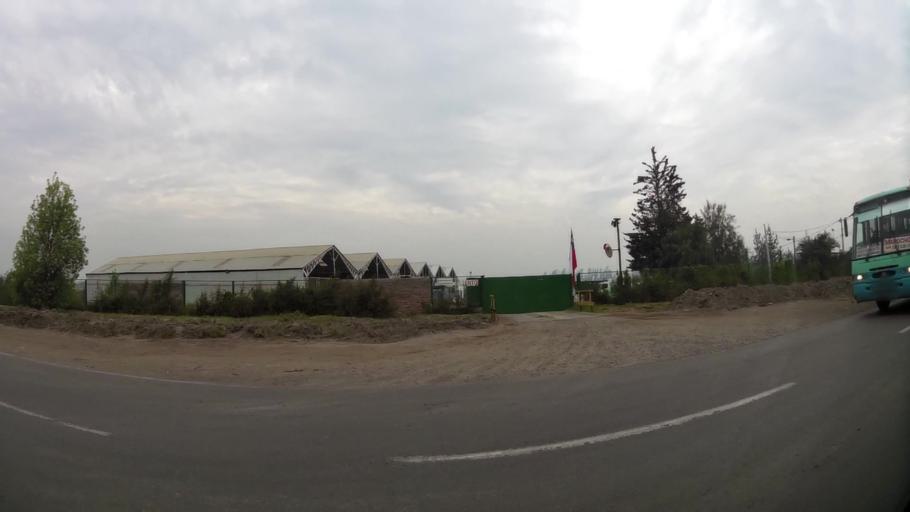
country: CL
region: Santiago Metropolitan
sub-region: Provincia de Chacabuco
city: Chicureo Abajo
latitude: -33.2619
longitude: -70.7582
